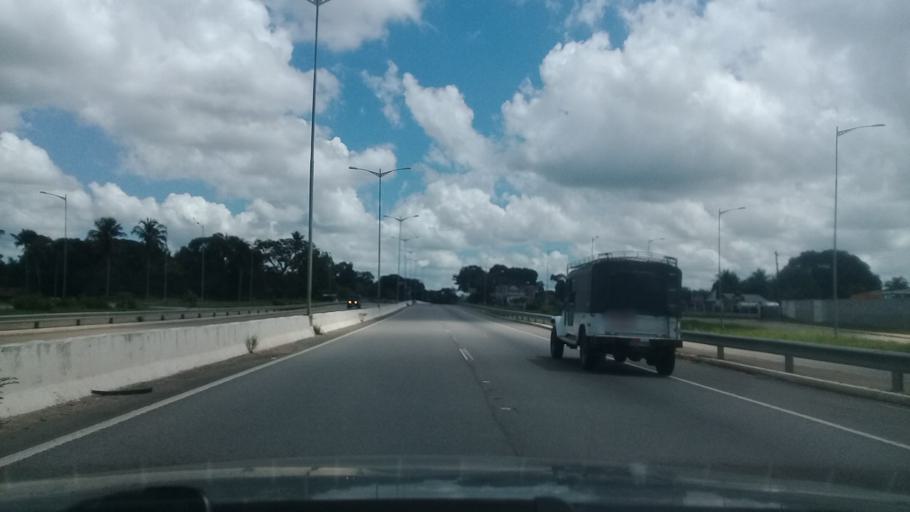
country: BR
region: Pernambuco
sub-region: Sao Lourenco Da Mata
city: Sao Lourenco da Mata
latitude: -7.9414
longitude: -35.1233
